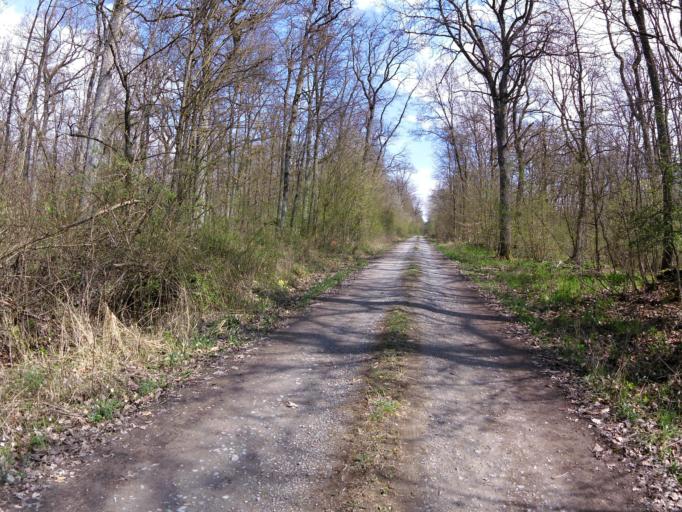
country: DE
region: Bavaria
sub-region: Regierungsbezirk Unterfranken
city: Rimpar
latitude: 49.8683
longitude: 9.9329
